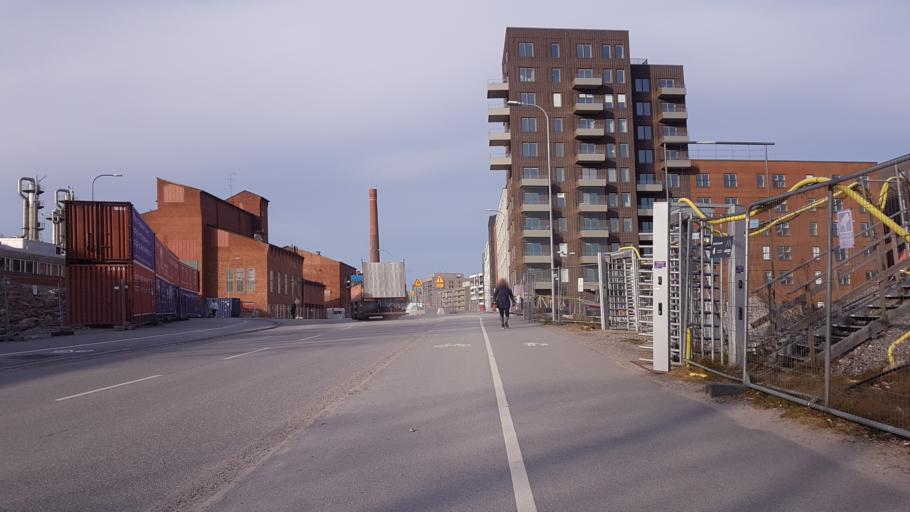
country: SE
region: Stockholm
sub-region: Stockholms Kommun
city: OEstermalm
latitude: 59.3600
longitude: 18.0982
